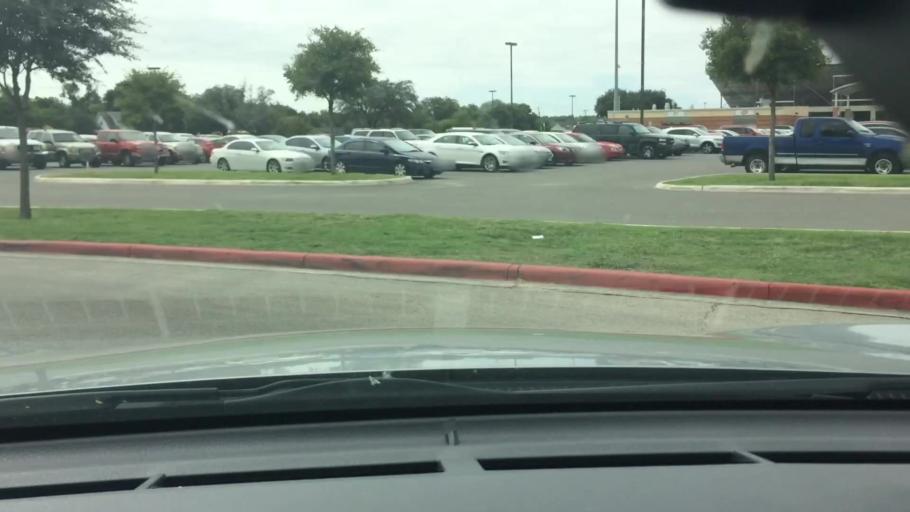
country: US
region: Texas
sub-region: Bexar County
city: Converse
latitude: 29.5090
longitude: -98.3036
